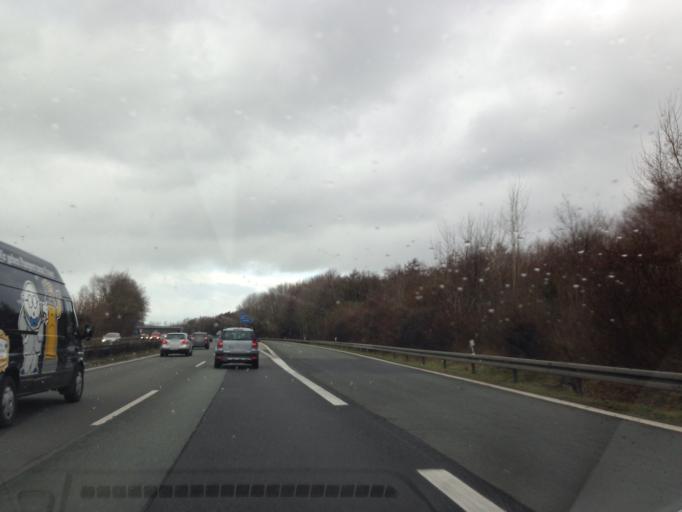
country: DE
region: North Rhine-Westphalia
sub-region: Regierungsbezirk Munster
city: Recklinghausen
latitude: 51.6482
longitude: 7.1717
